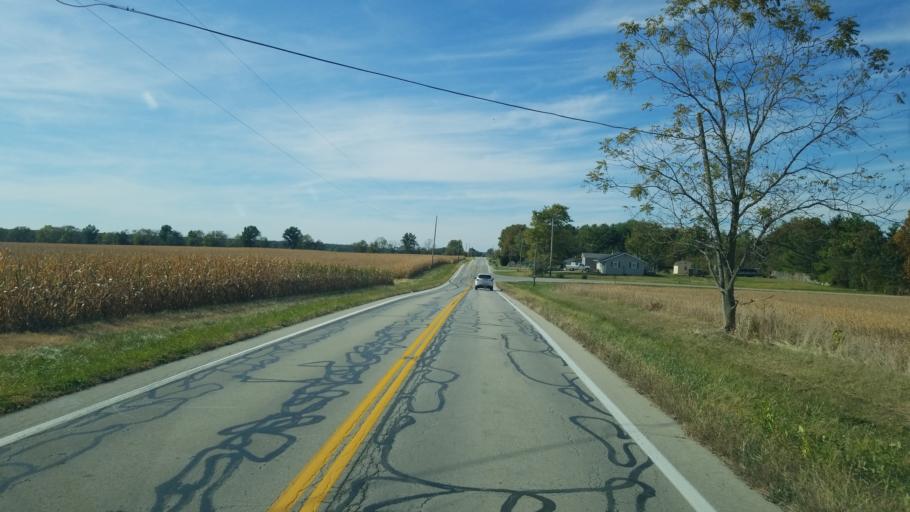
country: US
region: Ohio
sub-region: Clinton County
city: Wilmington
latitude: 39.3695
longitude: -83.8895
